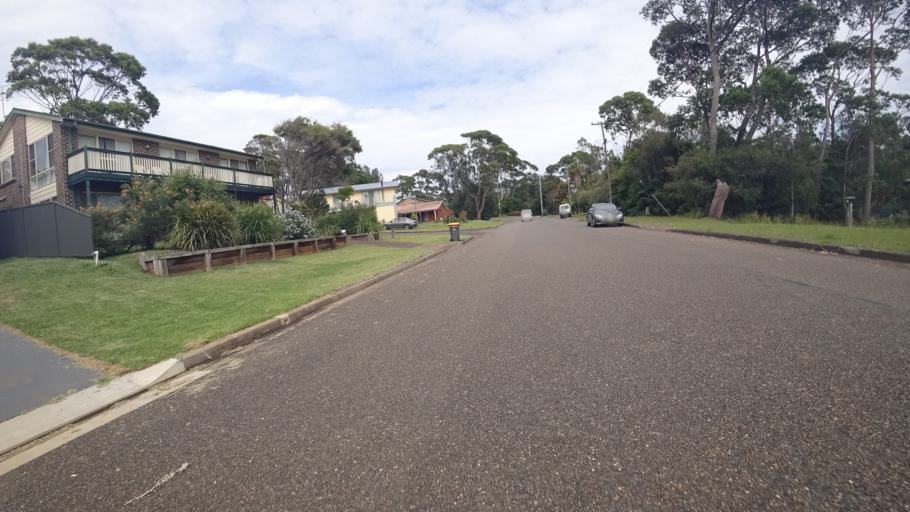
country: AU
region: New South Wales
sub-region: Shoalhaven Shire
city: Milton
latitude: -35.2558
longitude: 150.5226
